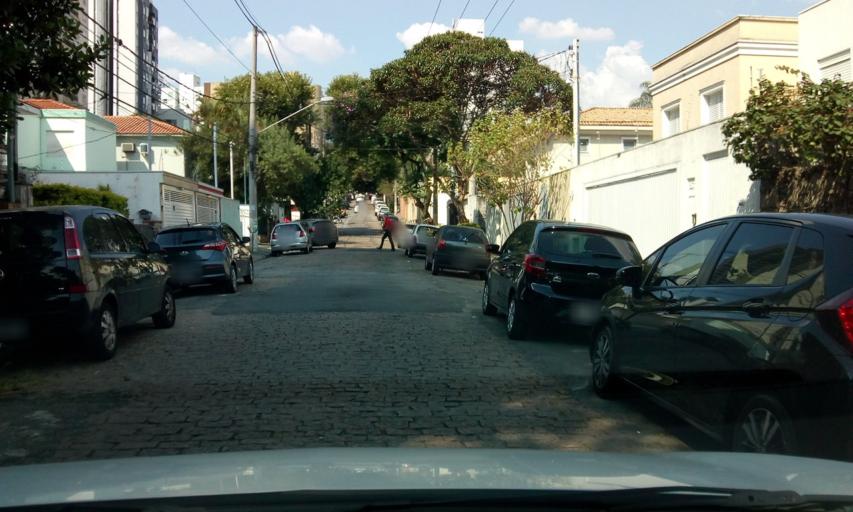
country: BR
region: Sao Paulo
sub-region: Sao Paulo
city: Sao Paulo
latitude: -23.6050
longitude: -46.6781
